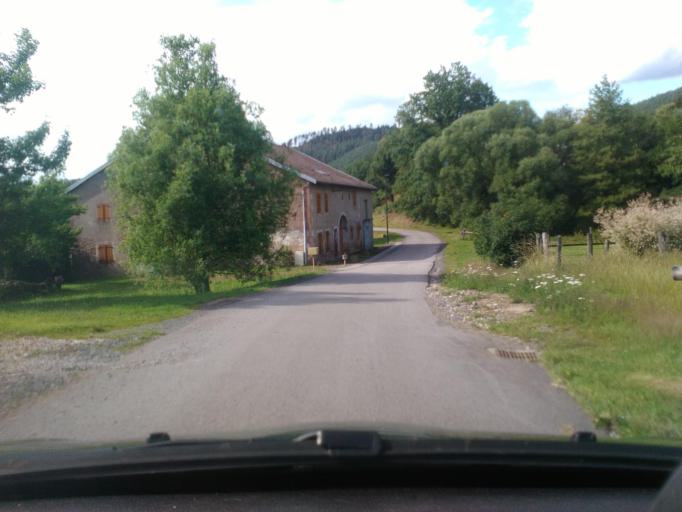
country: FR
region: Lorraine
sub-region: Departement des Vosges
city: Bruyeres
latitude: 48.2239
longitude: 6.7664
